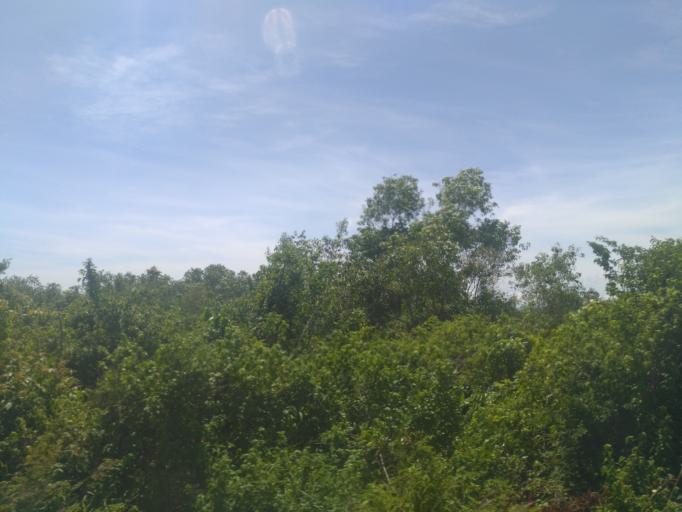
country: TZ
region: Zanzibar North
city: Gamba
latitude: -5.9257
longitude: 39.3520
